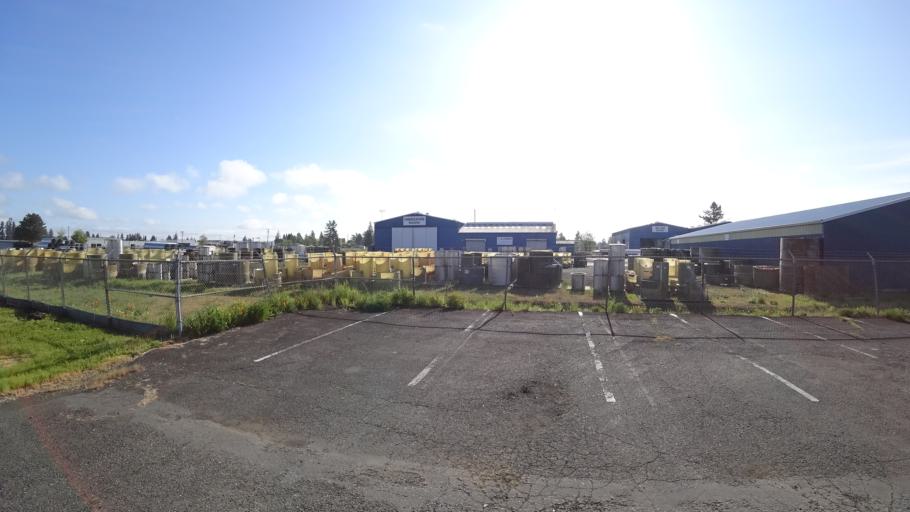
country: US
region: Oregon
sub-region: Washington County
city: Hillsboro
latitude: 45.5156
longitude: -123.0010
